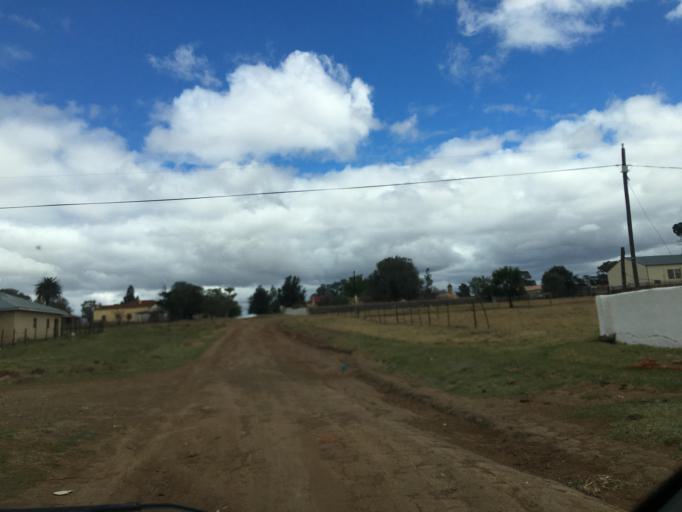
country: ZA
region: Eastern Cape
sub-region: Chris Hani District Municipality
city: Cala
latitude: -31.5224
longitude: 27.7026
